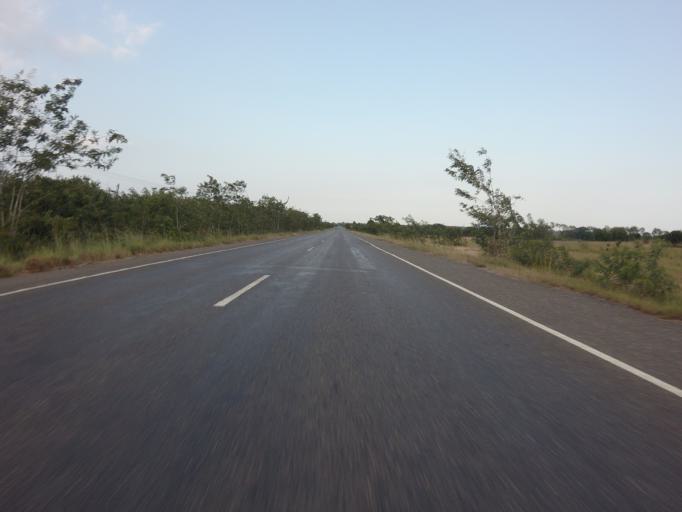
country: GH
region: Volta
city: Anloga
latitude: 6.0783
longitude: 0.5897
